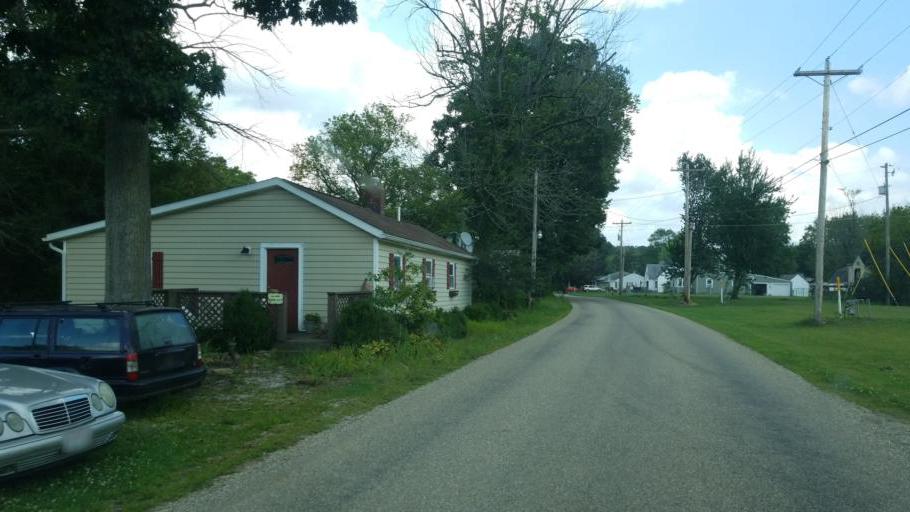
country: US
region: Ohio
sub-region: Knox County
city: Oak Hill
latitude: 40.3961
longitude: -82.2822
